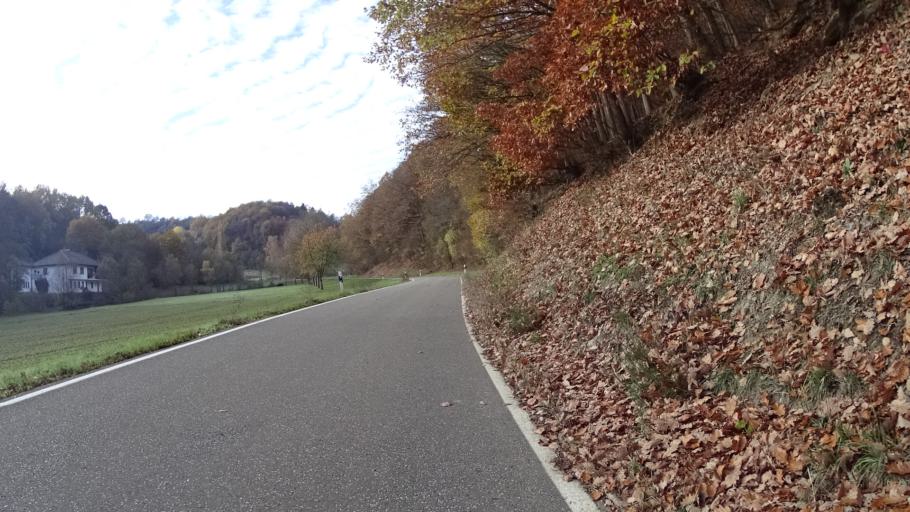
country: DE
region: Rheinland-Pfalz
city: Sankt Julian
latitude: 49.6166
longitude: 7.5062
